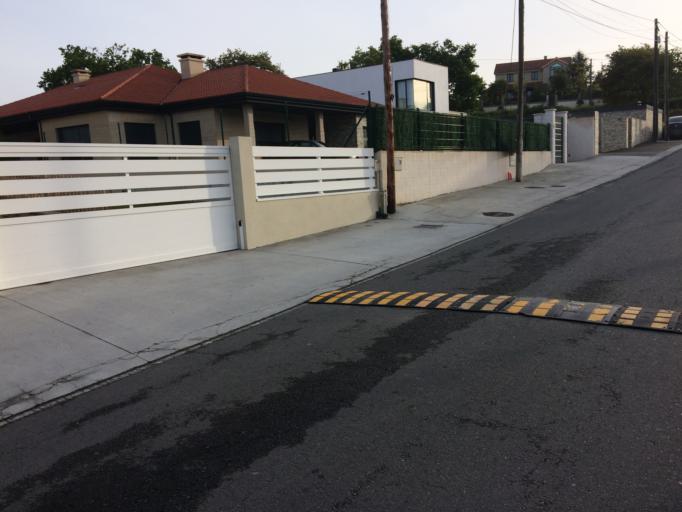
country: ES
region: Galicia
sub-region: Provincia da Coruna
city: Ames
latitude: 42.8330
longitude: -8.6052
